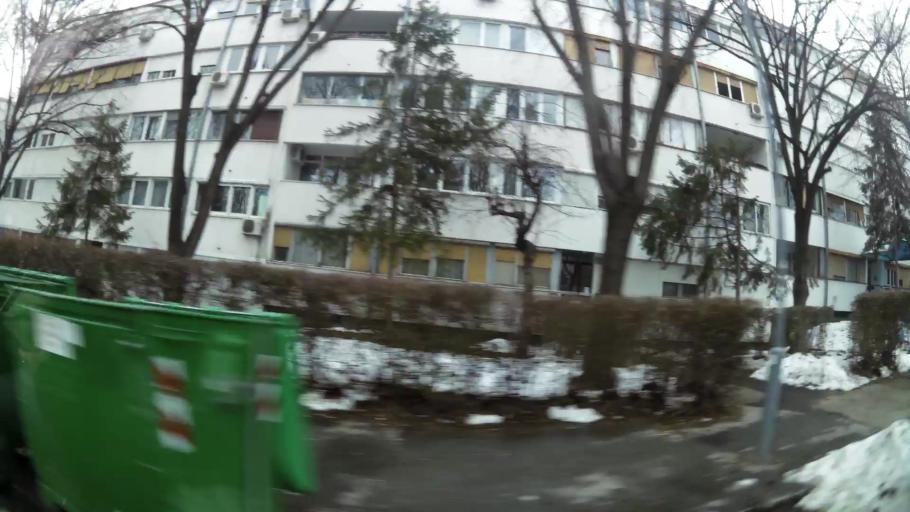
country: RS
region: Central Serbia
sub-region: Belgrade
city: Vozdovac
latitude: 44.7685
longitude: 20.4947
